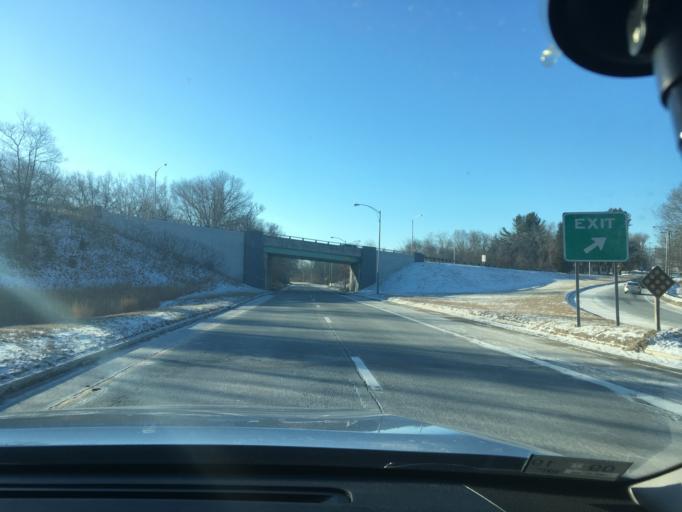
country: US
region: Rhode Island
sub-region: Kent County
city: West Warwick
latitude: 41.7365
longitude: -71.4806
